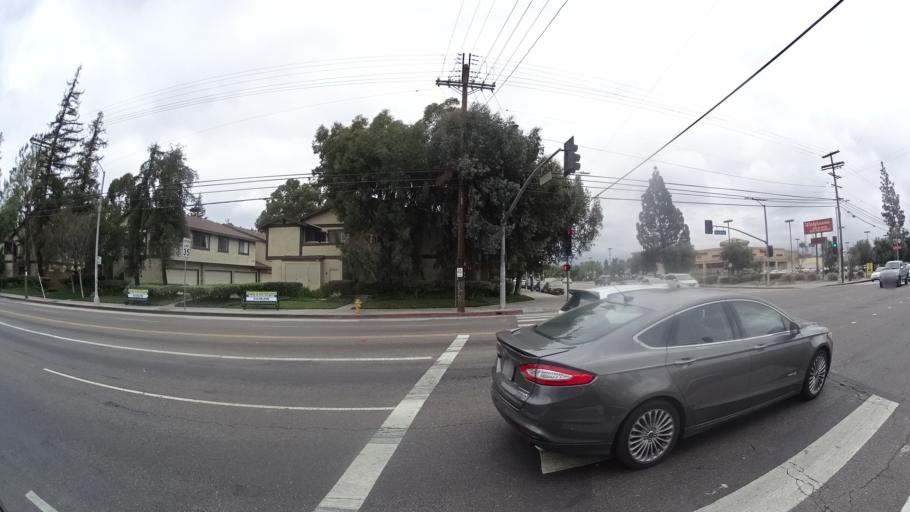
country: US
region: California
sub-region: Los Angeles County
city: San Fernando
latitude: 34.2469
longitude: -118.4483
